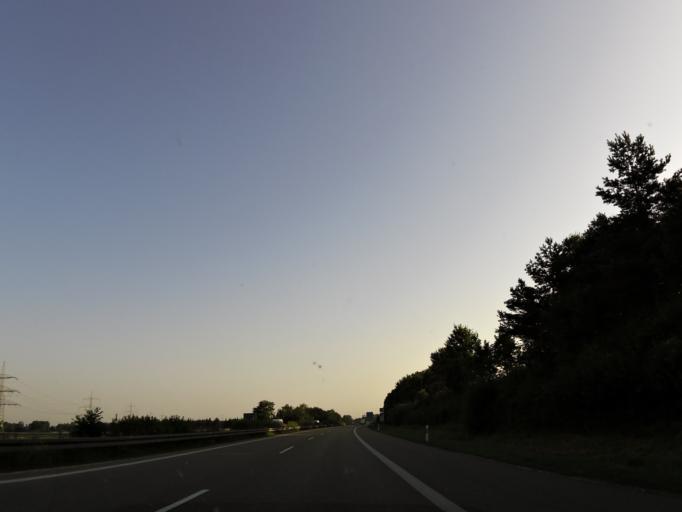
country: DE
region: Bavaria
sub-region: Swabia
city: Buxheim
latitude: 47.9880
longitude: 10.1505
